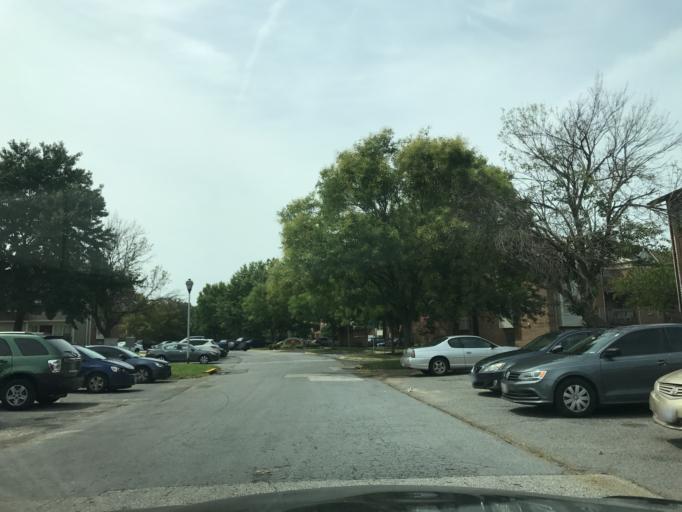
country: US
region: Maryland
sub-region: Baltimore County
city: Essex
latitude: 39.3026
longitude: -76.4521
